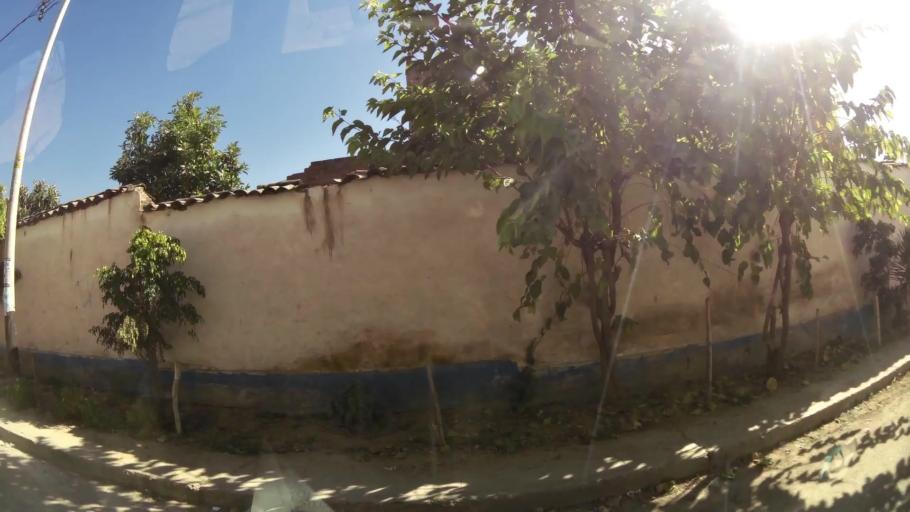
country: PE
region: Ayacucho
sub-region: Provincia de Huamanga
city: Ayacucho
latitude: -13.1623
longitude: -74.2331
